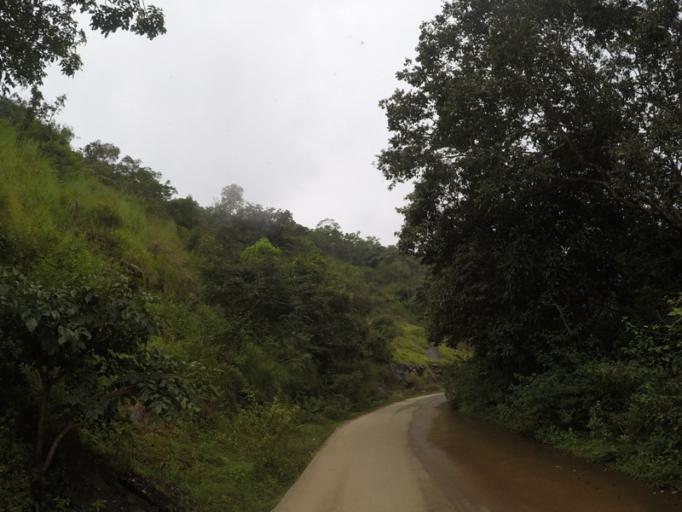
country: IN
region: Karnataka
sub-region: Chikmagalur
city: Mudigere
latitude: 13.1701
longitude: 75.4713
